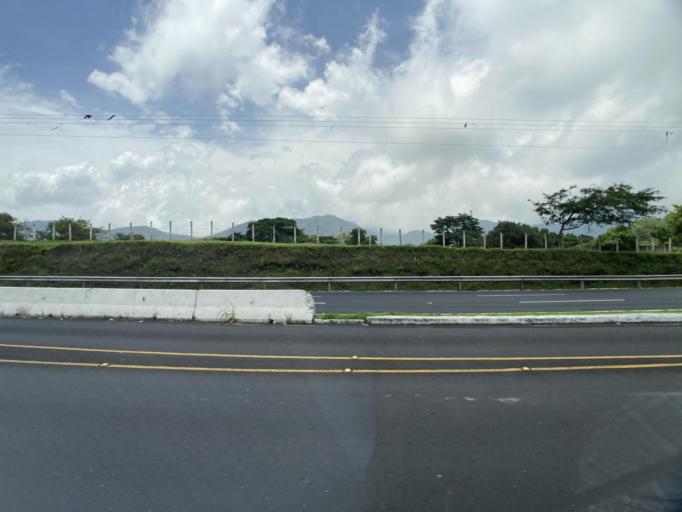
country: GT
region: Escuintla
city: Palin
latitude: 14.4082
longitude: -90.7027
